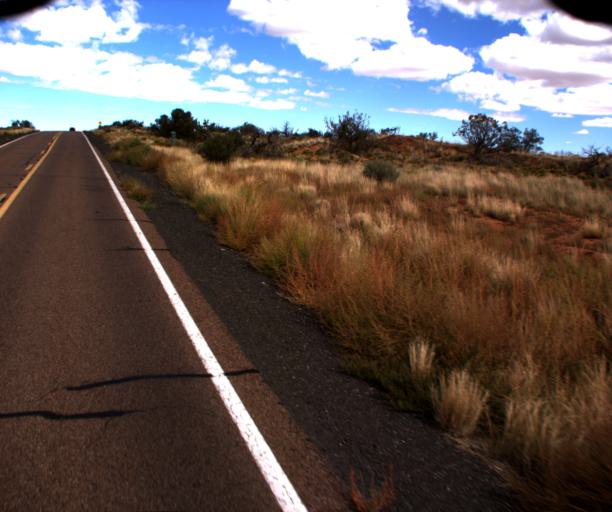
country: US
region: Arizona
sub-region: Navajo County
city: Heber-Overgaard
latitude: 34.6365
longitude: -110.3593
